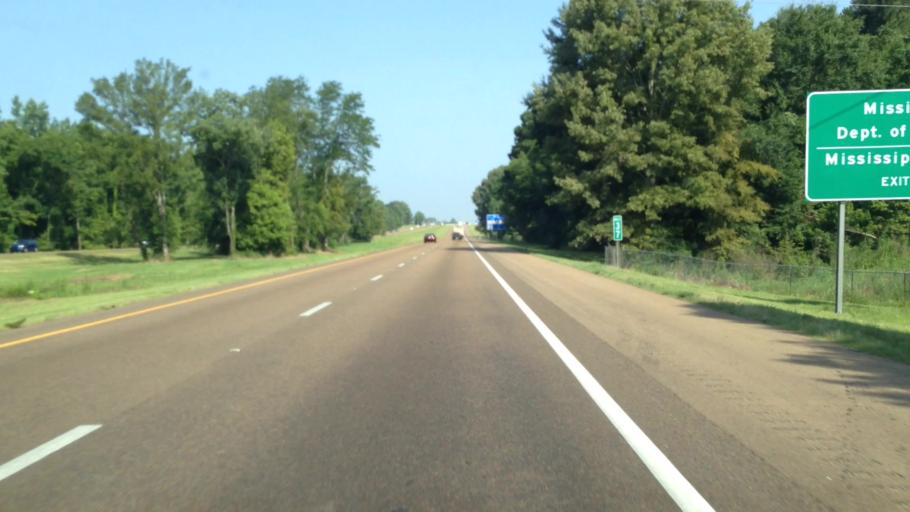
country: US
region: Mississippi
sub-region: Hinds County
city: Clinton
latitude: 32.3173
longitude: -90.3086
